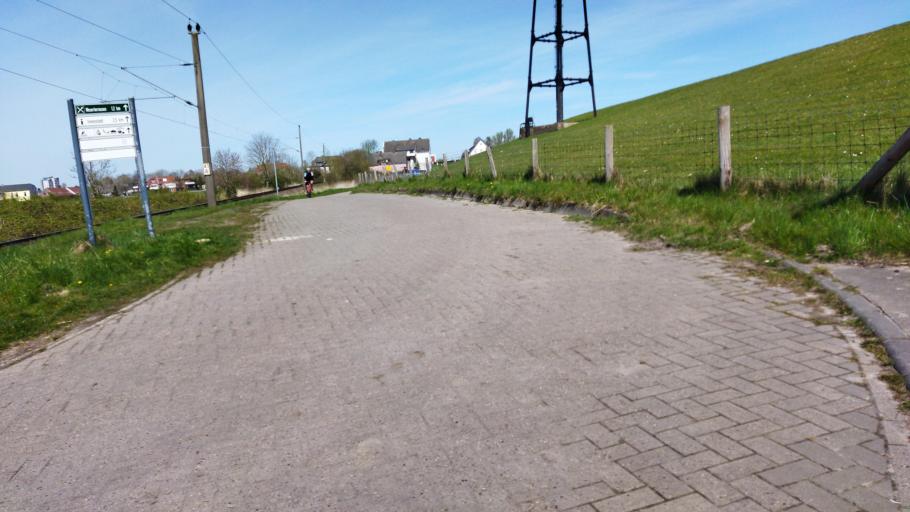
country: DE
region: Lower Saxony
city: Nordenham
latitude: 53.4647
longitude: 8.4758
